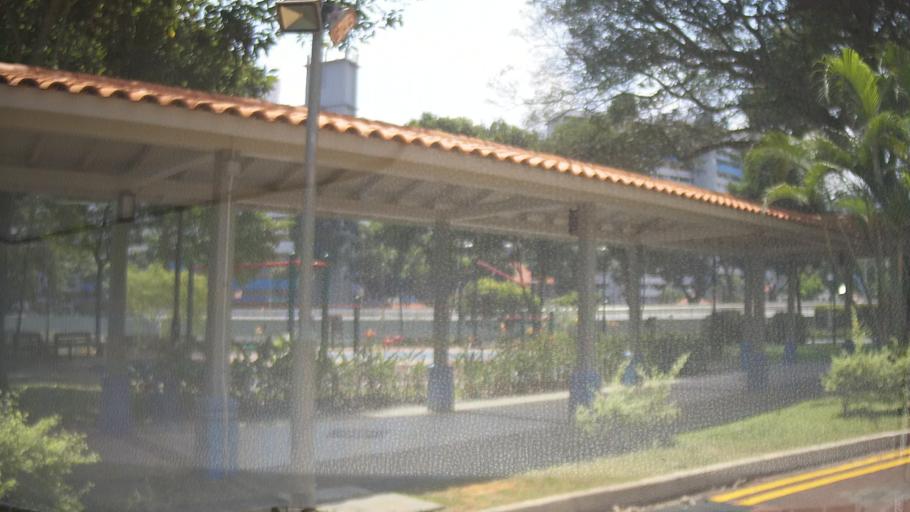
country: SG
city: Singapore
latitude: 1.3232
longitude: 103.8681
